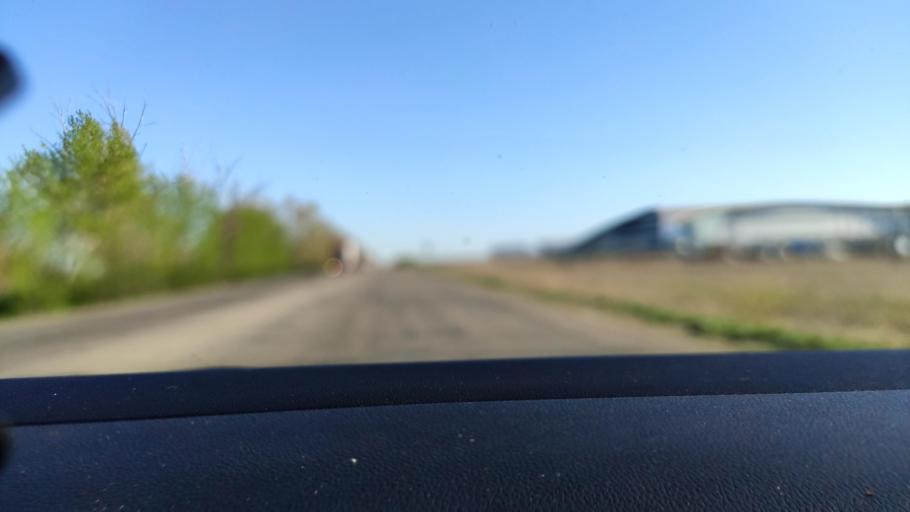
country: RU
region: Voronezj
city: Maslovka
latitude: 51.5438
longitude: 39.2854
